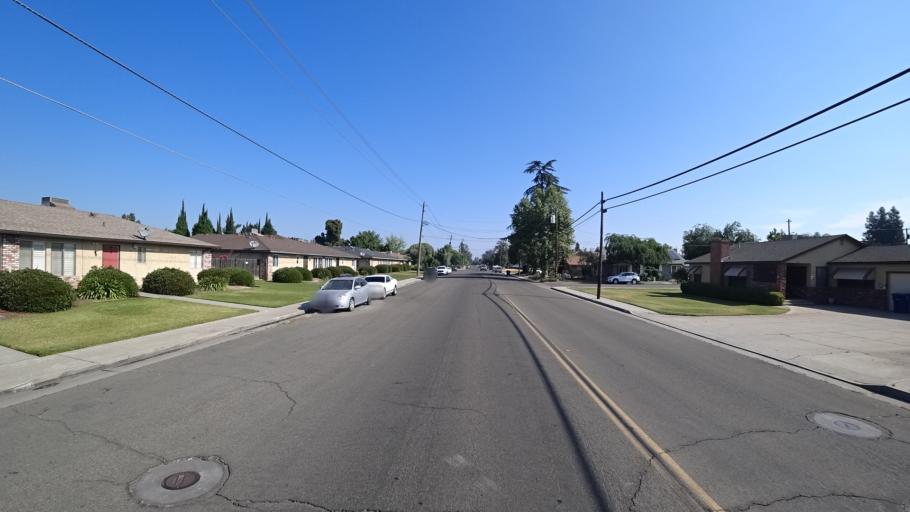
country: US
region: California
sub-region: Fresno County
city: Kingsburg
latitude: 36.5075
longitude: -119.5569
